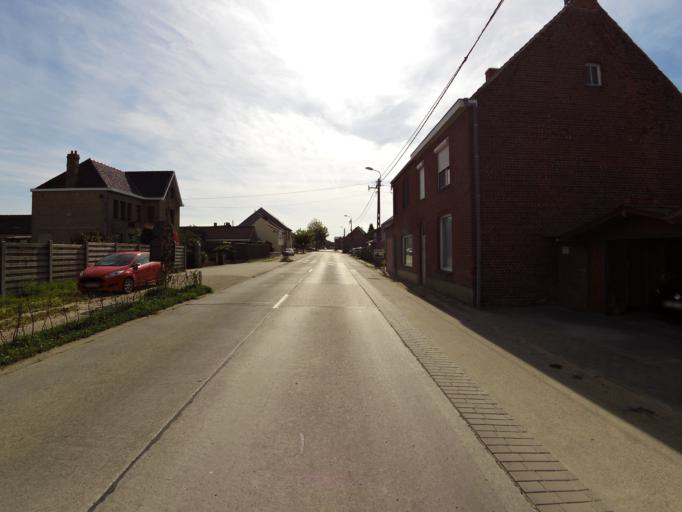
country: BE
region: Flanders
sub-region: Provincie West-Vlaanderen
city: Koekelare
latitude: 51.0904
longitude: 2.9653
